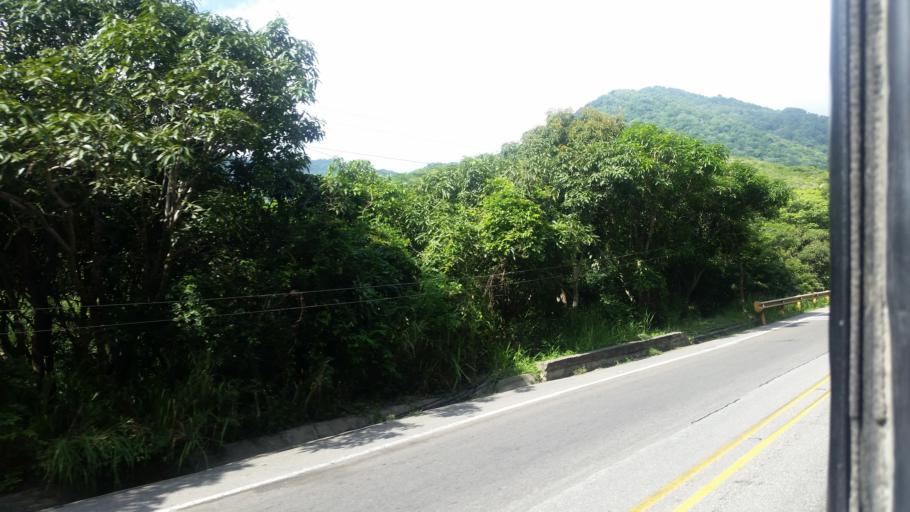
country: CO
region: Magdalena
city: Santa Marta
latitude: 11.2678
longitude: -74.0739
